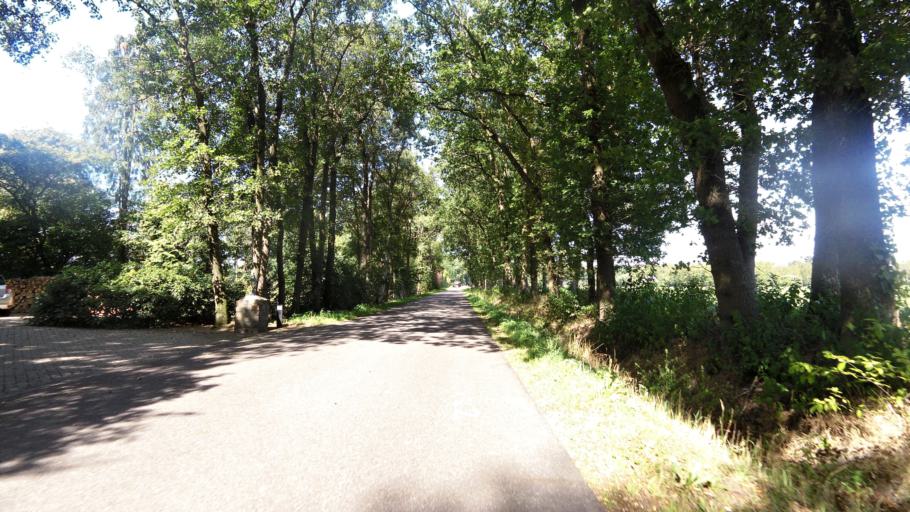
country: NL
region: Gelderland
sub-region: Gemeente Ede
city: Harskamp
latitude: 52.1220
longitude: 5.7485
